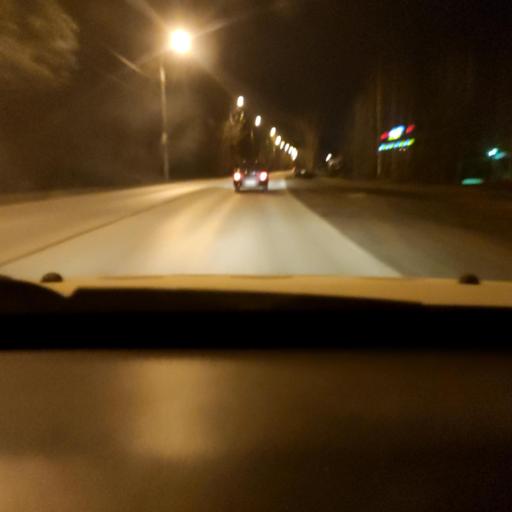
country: RU
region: Perm
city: Perm
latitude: 58.0697
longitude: 56.3470
